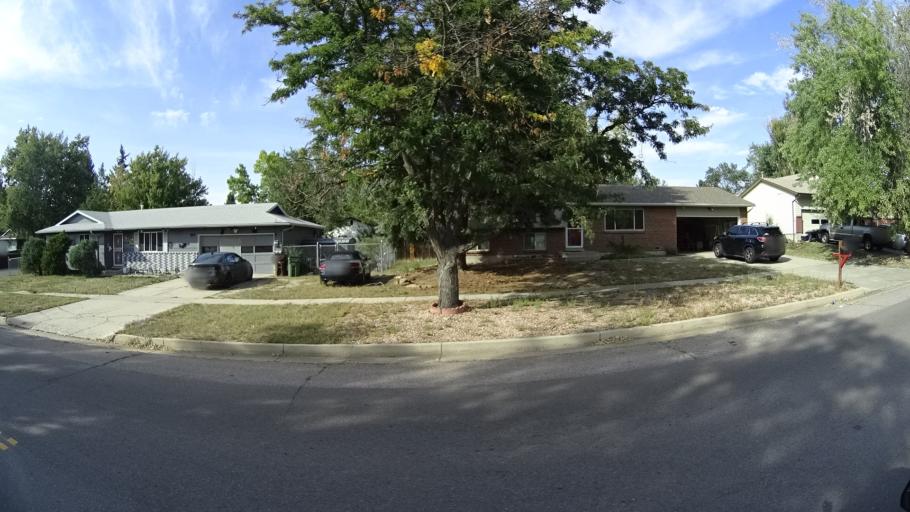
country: US
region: Colorado
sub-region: El Paso County
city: Cimarron Hills
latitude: 38.8971
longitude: -104.7696
